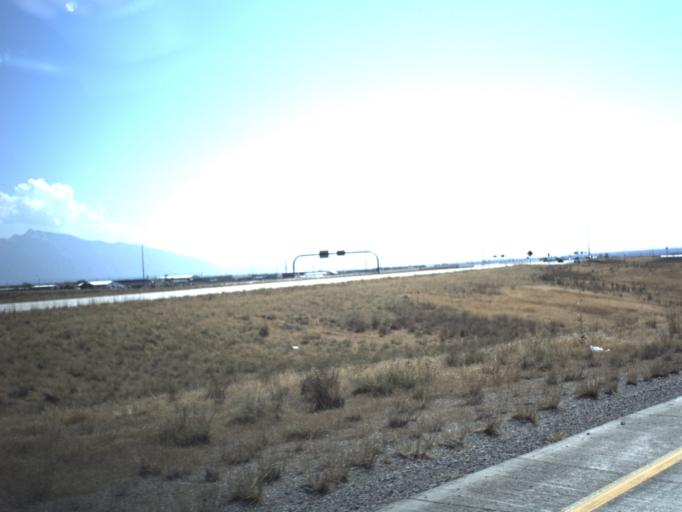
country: US
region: Utah
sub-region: Salt Lake County
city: West Valley City
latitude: 40.7681
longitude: -111.9874
